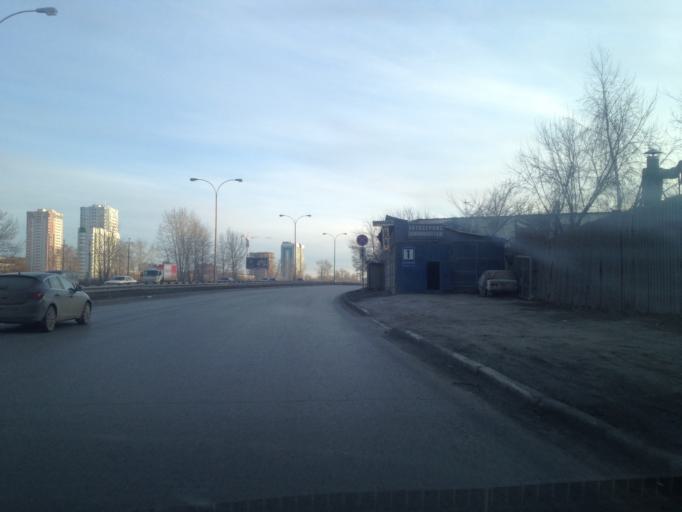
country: RU
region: Sverdlovsk
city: Yekaterinburg
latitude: 56.7923
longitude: 60.6389
